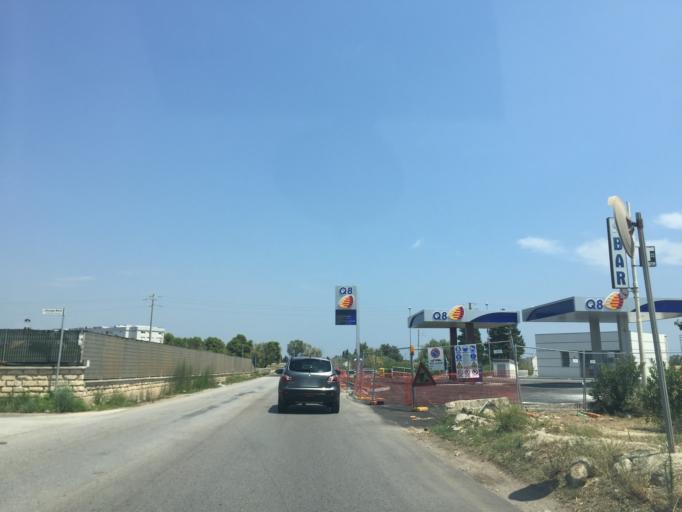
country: IT
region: Sicily
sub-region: Provincia di Siracusa
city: Avola
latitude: 36.9237
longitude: 15.1563
